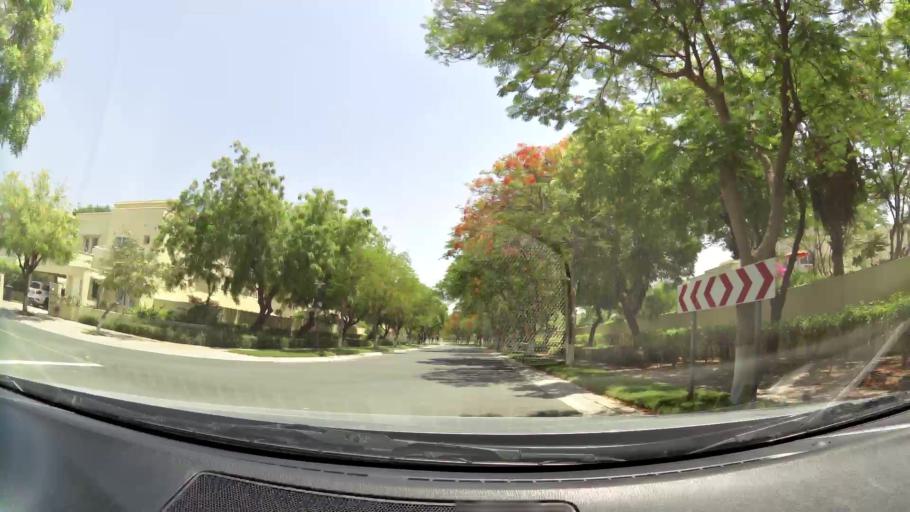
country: AE
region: Dubai
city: Dubai
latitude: 25.0432
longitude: 55.1735
